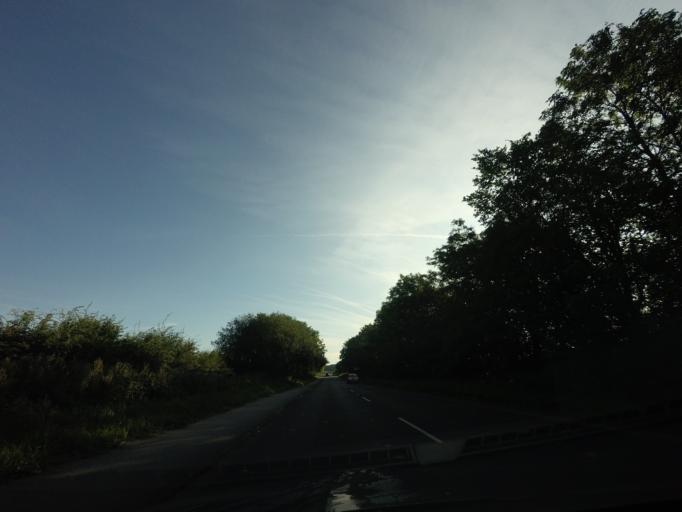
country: GB
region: England
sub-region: Derbyshire
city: Pinxton
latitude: 53.0605
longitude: -1.2804
